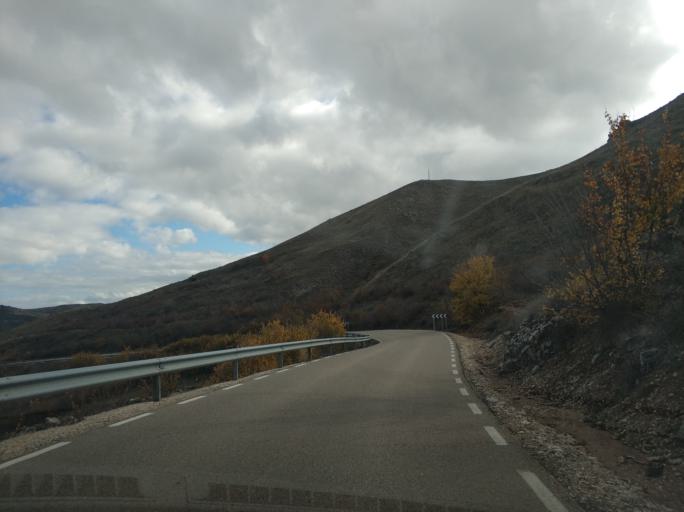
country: ES
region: Castille and Leon
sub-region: Provincia de Soria
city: Medinaceli
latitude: 41.1636
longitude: -2.4305
